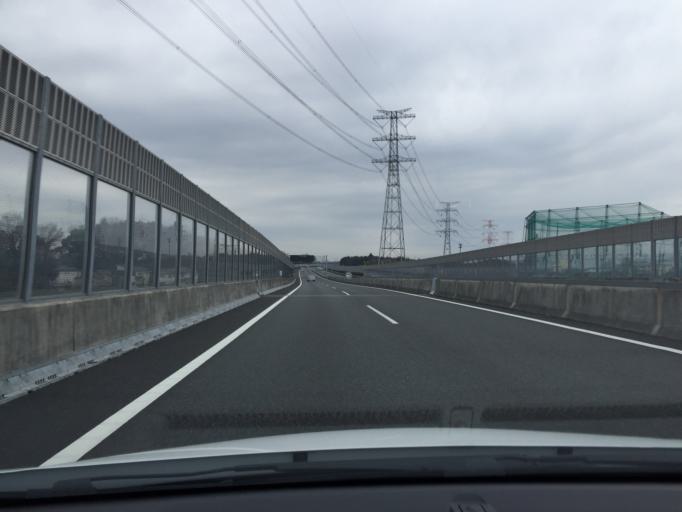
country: JP
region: Saitama
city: Sakado
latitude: 35.9451
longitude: 139.4144
